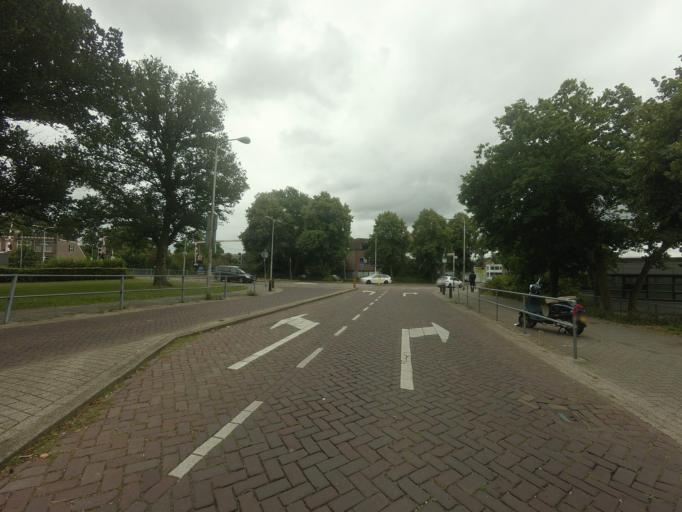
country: NL
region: North Holland
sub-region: Gemeente Bloemendaal
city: Bloemendaal
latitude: 52.4190
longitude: 4.6309
